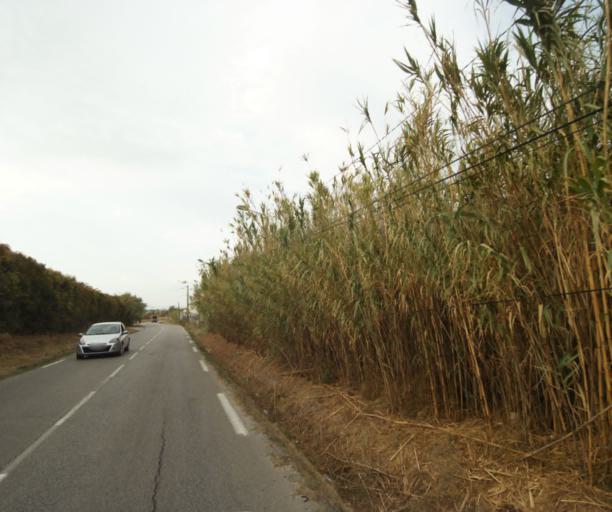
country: FR
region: Provence-Alpes-Cote d'Azur
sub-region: Departement des Bouches-du-Rhone
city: Gignac-la-Nerthe
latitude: 43.3990
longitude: 5.2183
